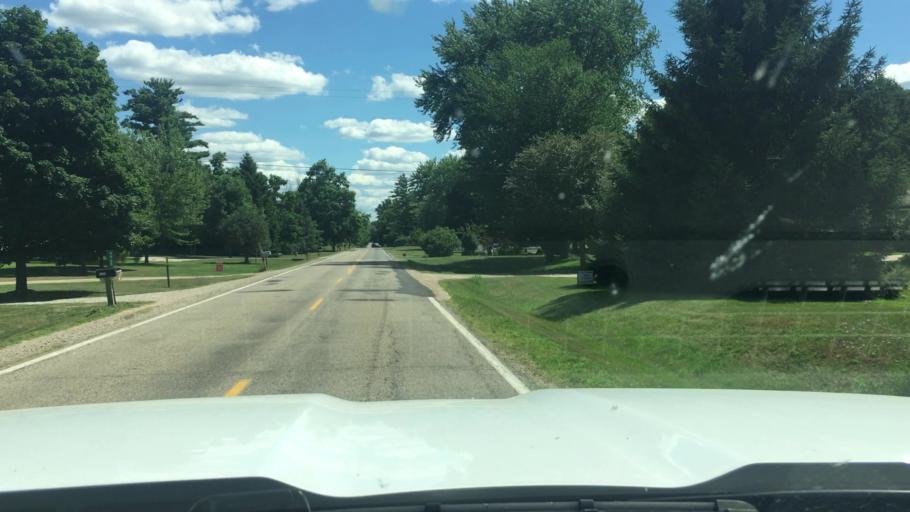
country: US
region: Michigan
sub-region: Kent County
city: Sparta
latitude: 43.1455
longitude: -85.6409
